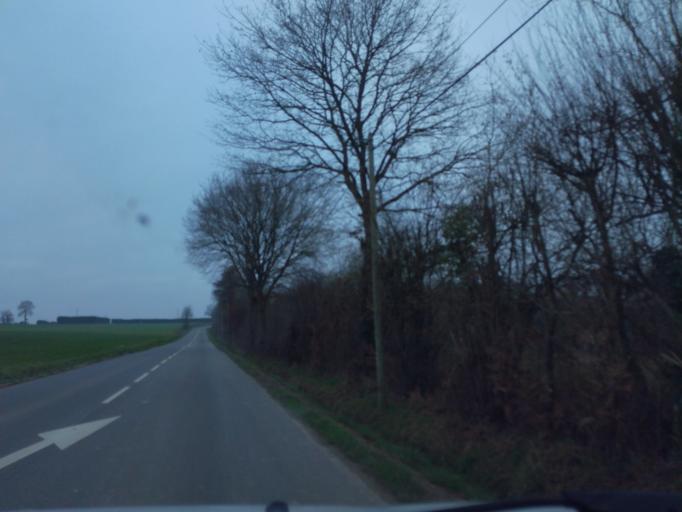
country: FR
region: Brittany
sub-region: Departement d'Ille-et-Vilaine
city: Gosne
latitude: 48.2527
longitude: -1.4569
